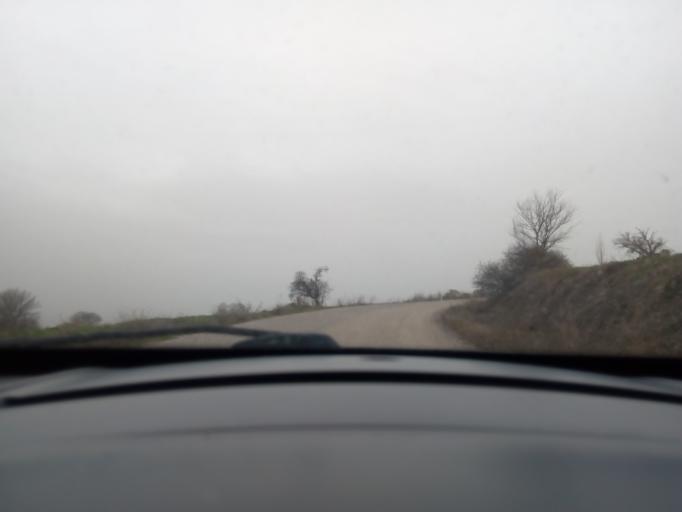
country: TR
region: Balikesir
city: Susurluk
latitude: 39.9104
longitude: 28.1176
